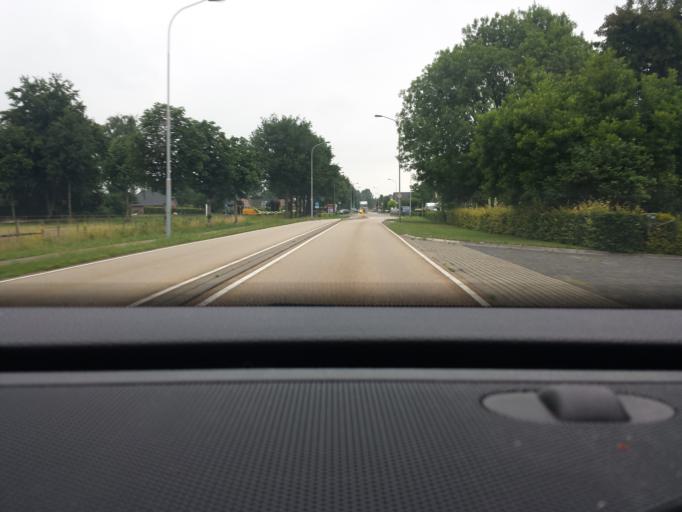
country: NL
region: Gelderland
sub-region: Gemeente Bronckhorst
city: Hengelo
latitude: 52.0092
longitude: 6.3063
